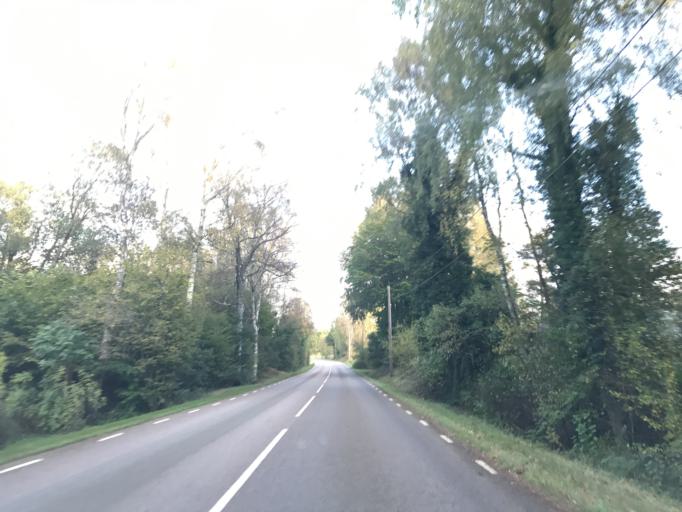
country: SE
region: Skane
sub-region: Klippans Kommun
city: Ljungbyhed
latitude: 56.1385
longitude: 13.2329
